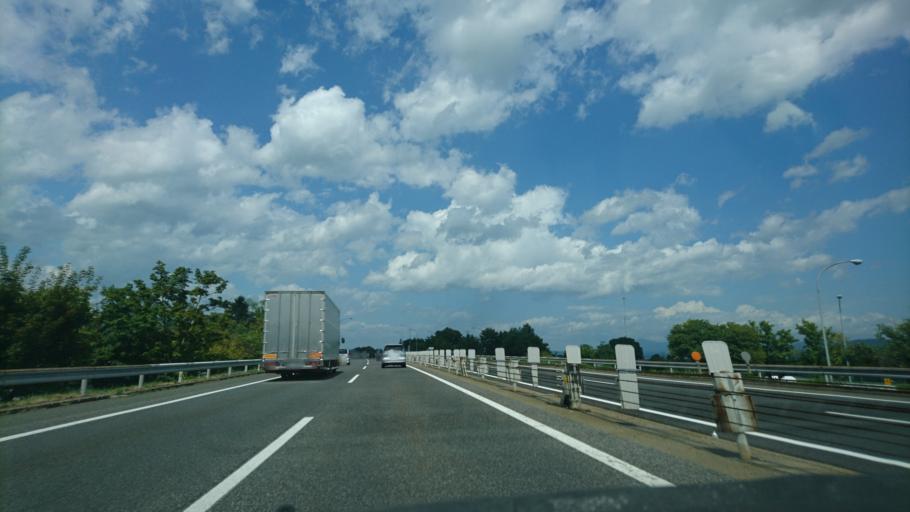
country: JP
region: Iwate
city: Morioka-shi
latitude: 39.6186
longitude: 141.1299
